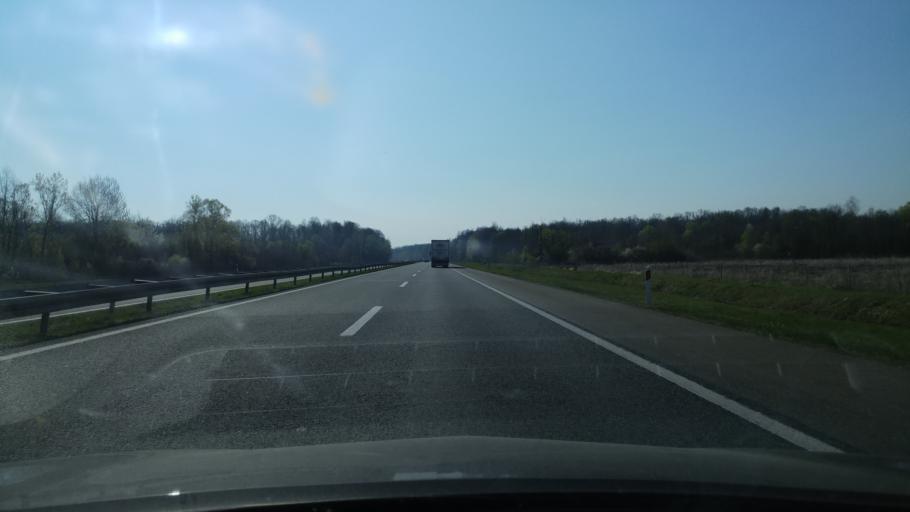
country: HR
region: Sisacko-Moslavacka
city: Lipovljani
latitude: 45.3484
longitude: 16.9146
